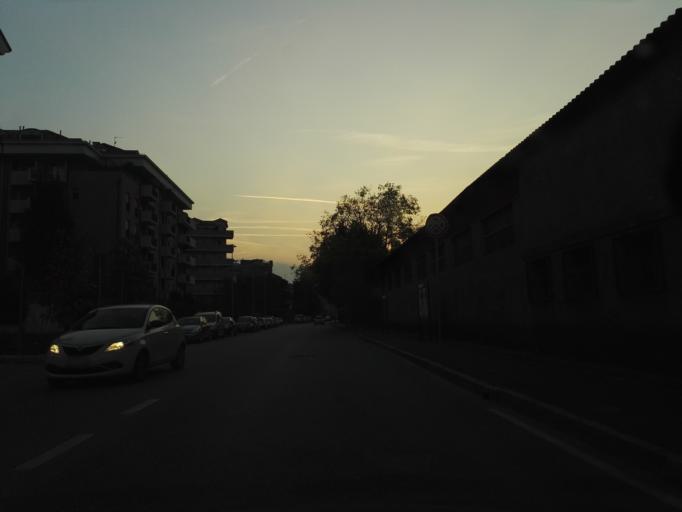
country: IT
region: Lombardy
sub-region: Citta metropolitana di Milano
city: San Giuliano Milanese
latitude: 45.4036
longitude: 9.2805
